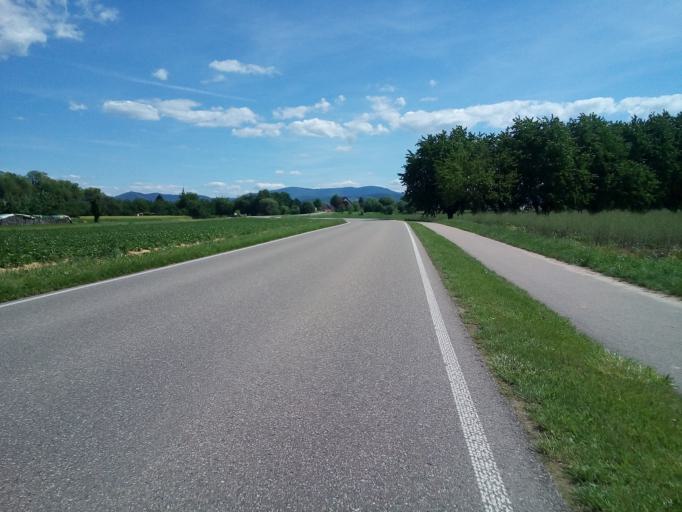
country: DE
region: Baden-Wuerttemberg
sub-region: Freiburg Region
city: Renchen
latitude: 48.5742
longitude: 8.0165
